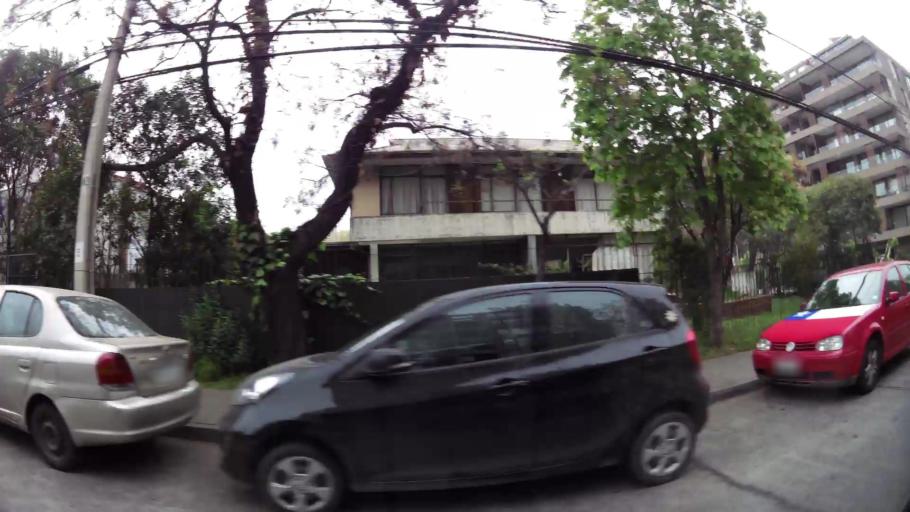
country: CL
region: Santiago Metropolitan
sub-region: Provincia de Santiago
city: Villa Presidente Frei, Nunoa, Santiago, Chile
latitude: -33.4003
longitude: -70.5858
